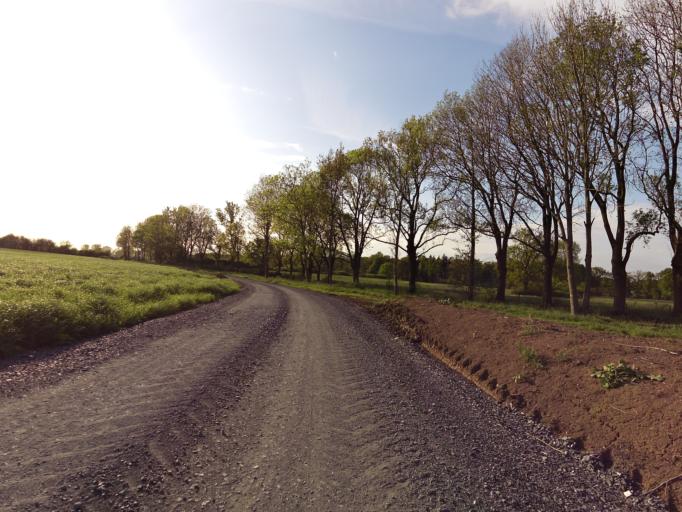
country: NL
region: Gelderland
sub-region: Gemeente Montferland
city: s-Heerenberg
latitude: 51.8687
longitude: 6.2417
